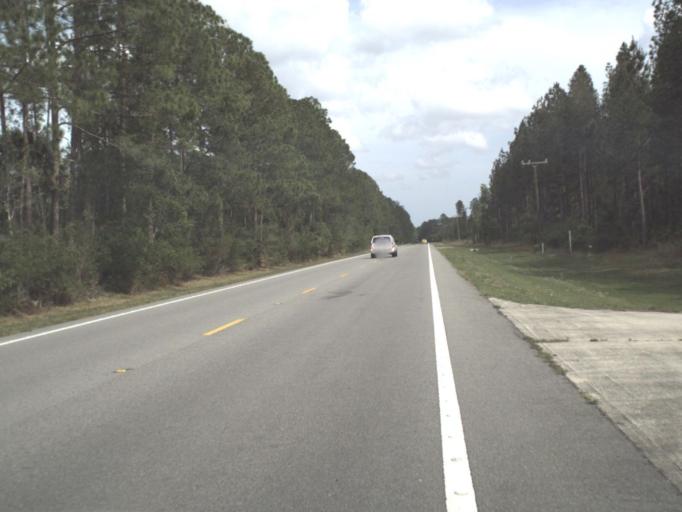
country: US
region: Florida
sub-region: Flagler County
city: Bunnell
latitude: 29.4736
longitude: -81.3270
